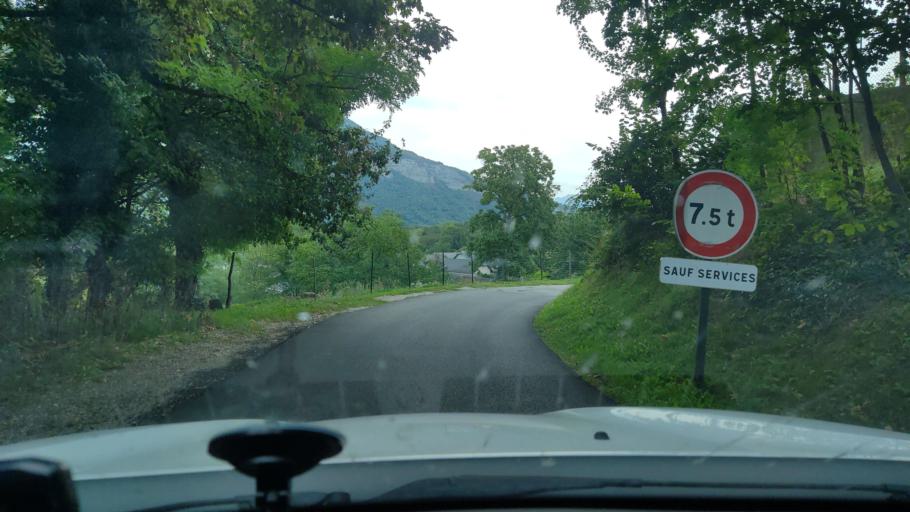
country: FR
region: Rhone-Alpes
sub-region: Departement de la Savoie
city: Voglans
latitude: 45.6305
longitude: 5.9082
